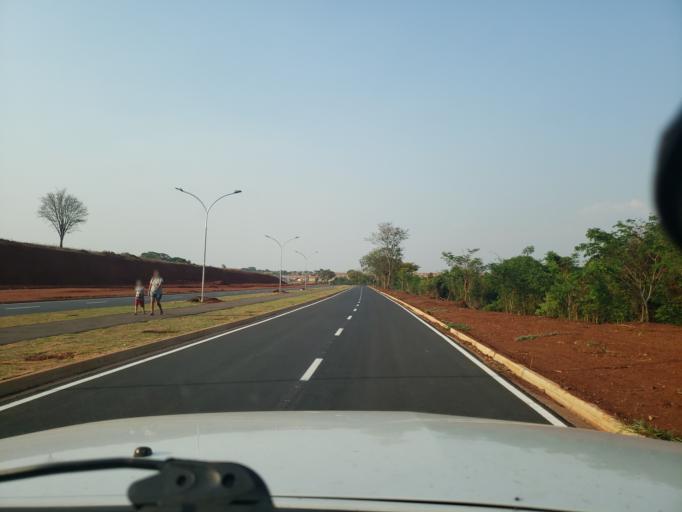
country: BR
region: Sao Paulo
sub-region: Moji-Guacu
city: Mogi-Gaucu
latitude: -22.3221
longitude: -46.9477
